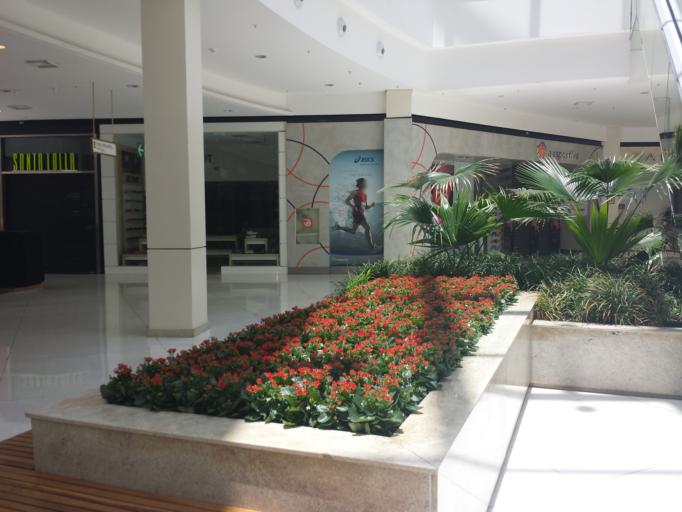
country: BR
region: Federal District
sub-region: Brasilia
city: Brasilia
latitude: -15.7208
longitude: -47.8858
